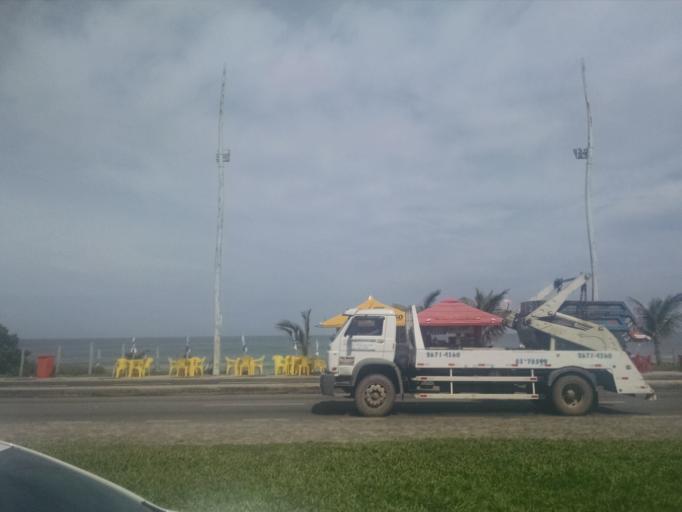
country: BR
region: Rio de Janeiro
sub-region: Rio De Janeiro
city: Rio de Janeiro
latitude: -23.0102
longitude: -43.3447
